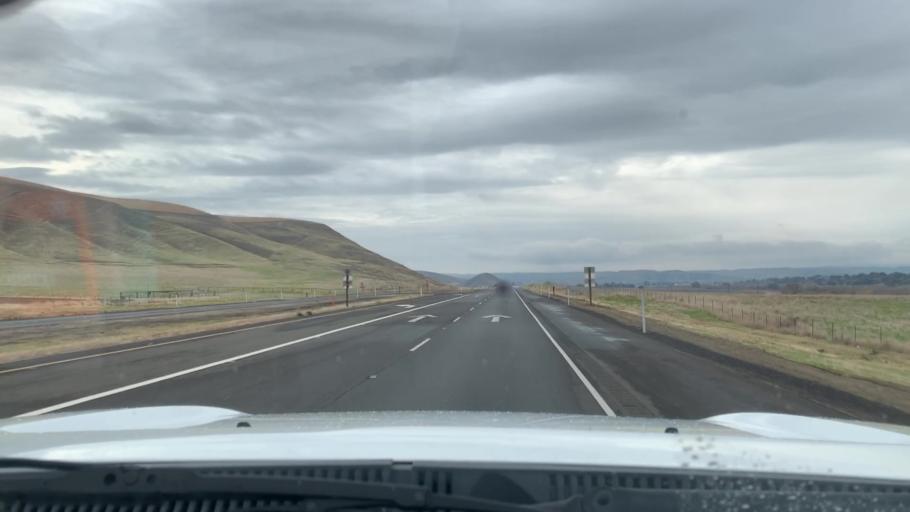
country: US
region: California
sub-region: San Luis Obispo County
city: Shandon
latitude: 35.6590
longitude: -120.4546
